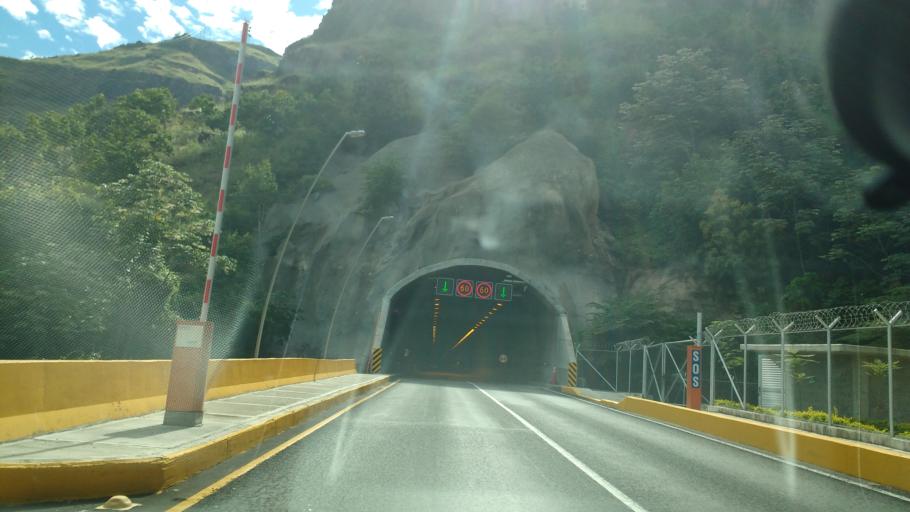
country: CO
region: Tolima
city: Valle de San Juan
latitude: 4.2865
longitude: -75.0239
